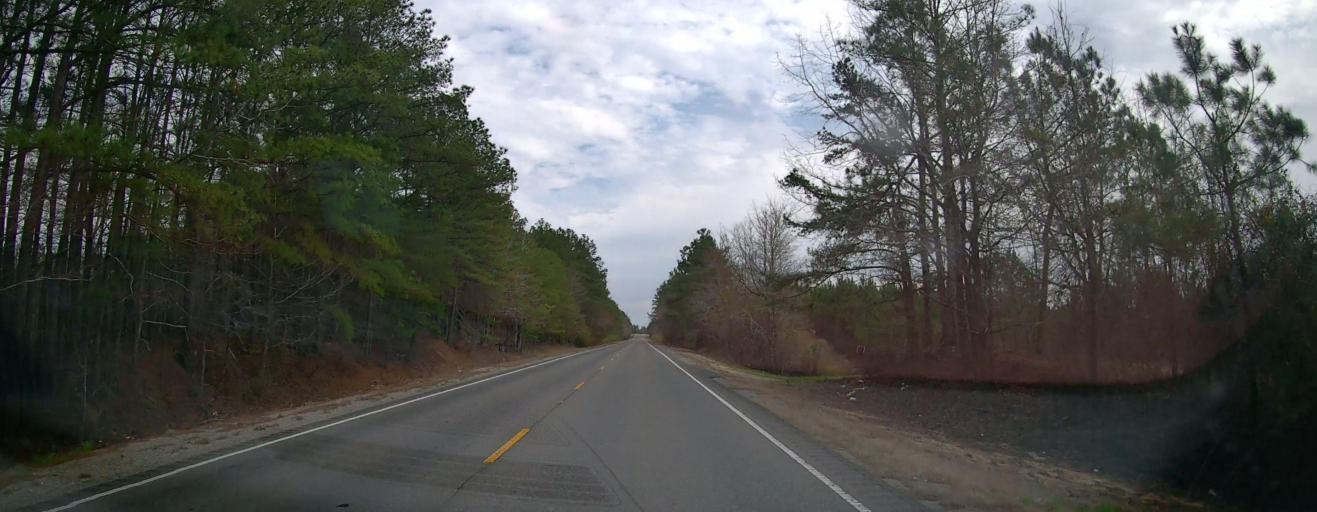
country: US
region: Alabama
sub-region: Marion County
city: Guin
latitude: 34.0451
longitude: -87.9591
